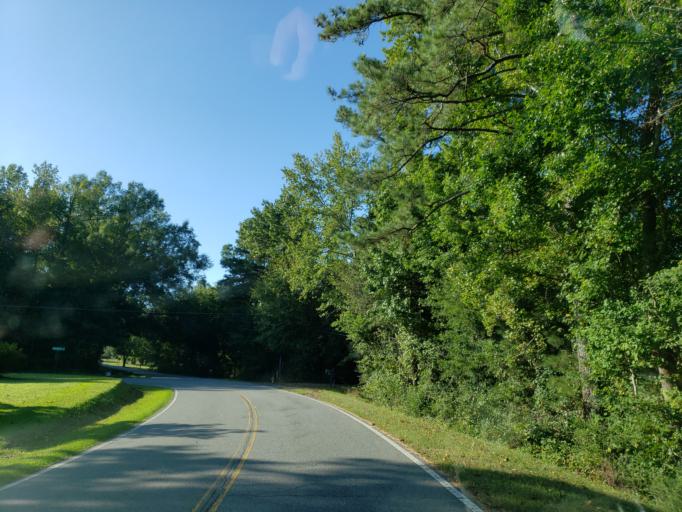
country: US
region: Georgia
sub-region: Bartow County
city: Rydal
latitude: 34.2939
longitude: -84.7543
